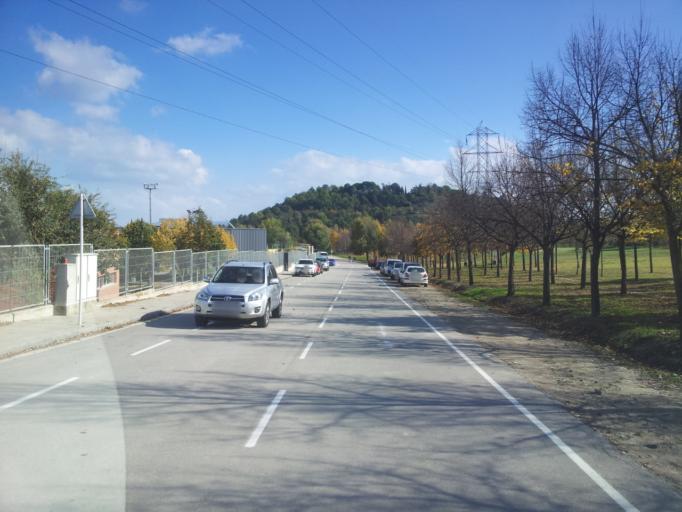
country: ES
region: Catalonia
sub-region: Provincia de Barcelona
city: Vic
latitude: 41.9360
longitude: 2.2390
